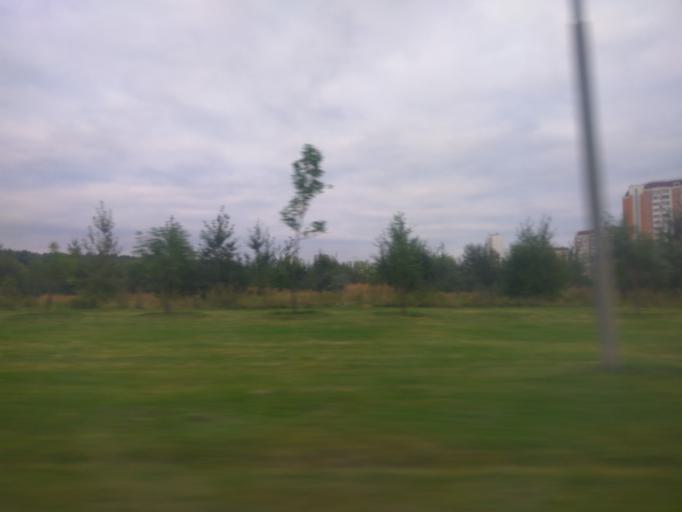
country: RU
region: Moscow
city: Zhulebino
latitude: 55.7170
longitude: 37.8763
